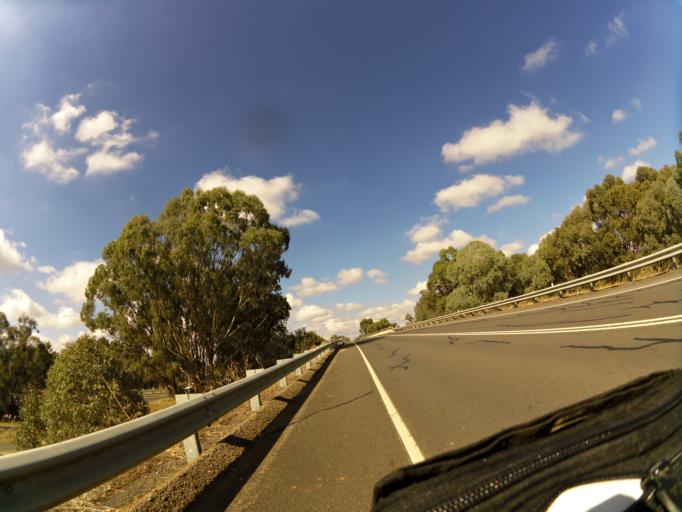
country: AU
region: Victoria
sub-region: Benalla
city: Benalla
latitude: -36.5724
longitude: 145.9917
